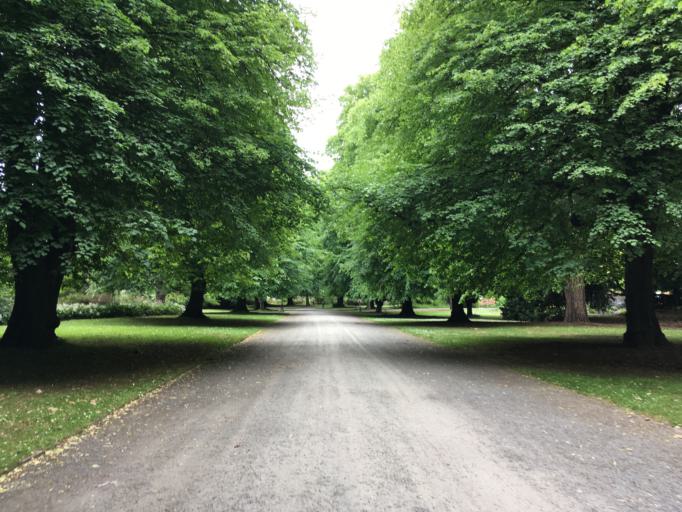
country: NZ
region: Canterbury
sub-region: Christchurch City
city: Christchurch
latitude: -43.5310
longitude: 172.6201
